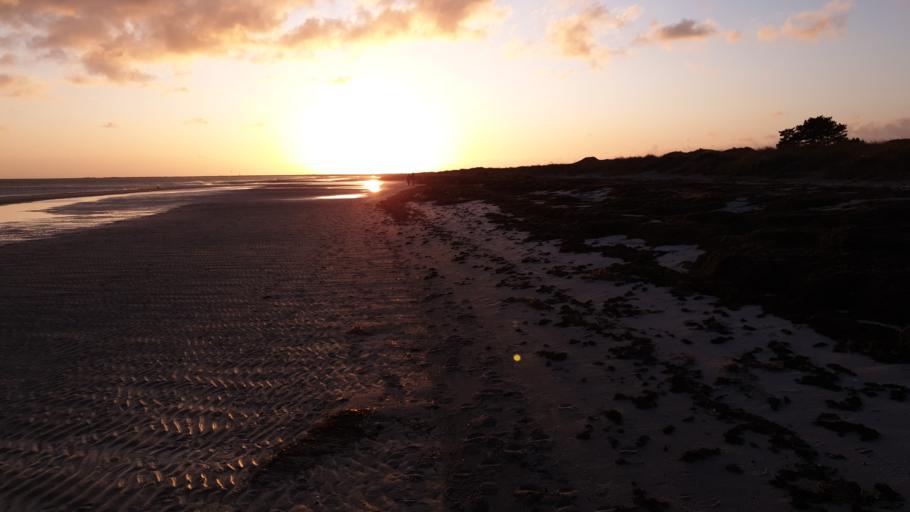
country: SE
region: Skane
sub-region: Vellinge Kommun
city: Skanor med Falsterbo
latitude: 55.3822
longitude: 12.8241
